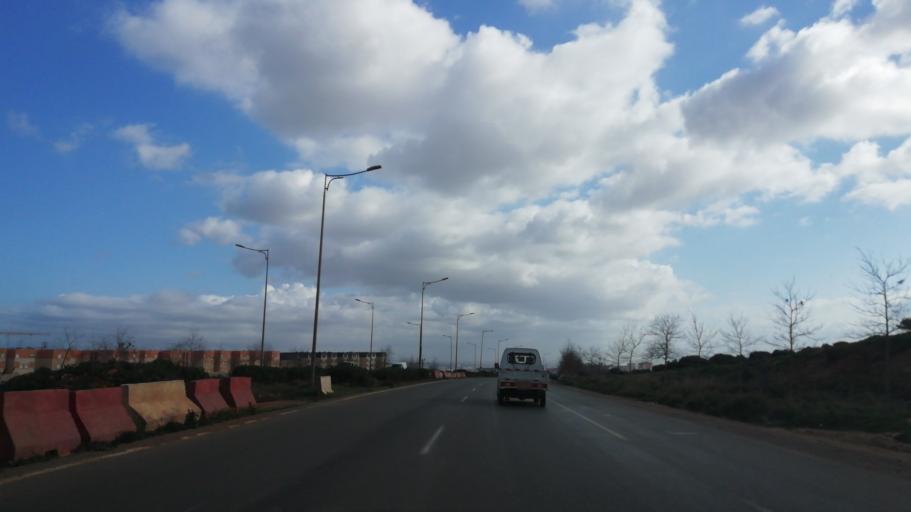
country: DZ
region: Oran
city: Oran
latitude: 35.6525
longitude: -0.6861
